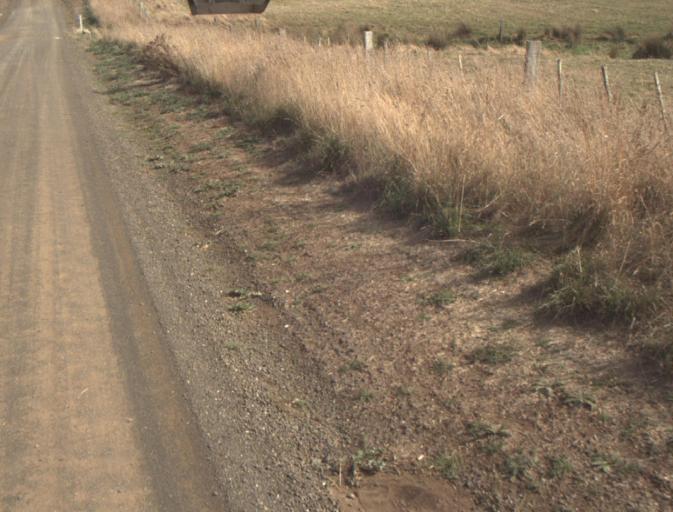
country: AU
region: Tasmania
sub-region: Launceston
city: Mayfield
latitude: -41.1870
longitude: 147.1911
